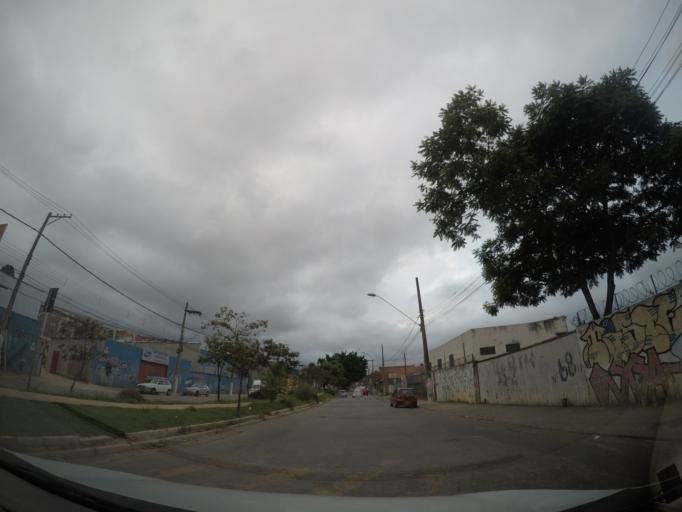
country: BR
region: Sao Paulo
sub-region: Aruja
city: Aruja
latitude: -23.4100
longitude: -46.4122
